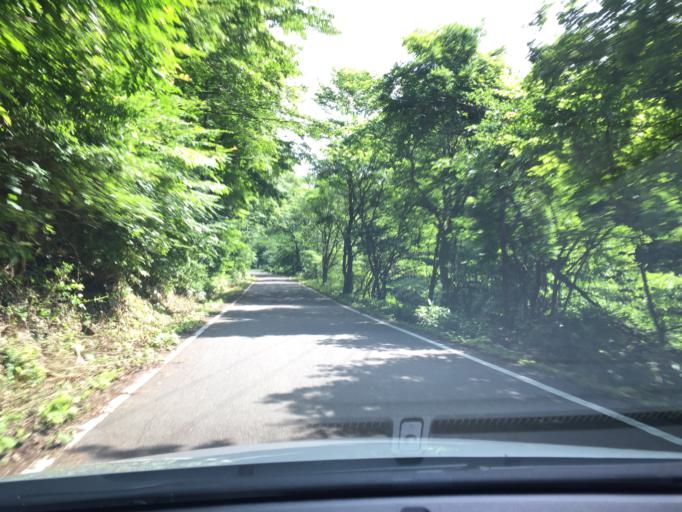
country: JP
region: Fukushima
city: Inawashiro
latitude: 37.2870
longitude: 140.0644
